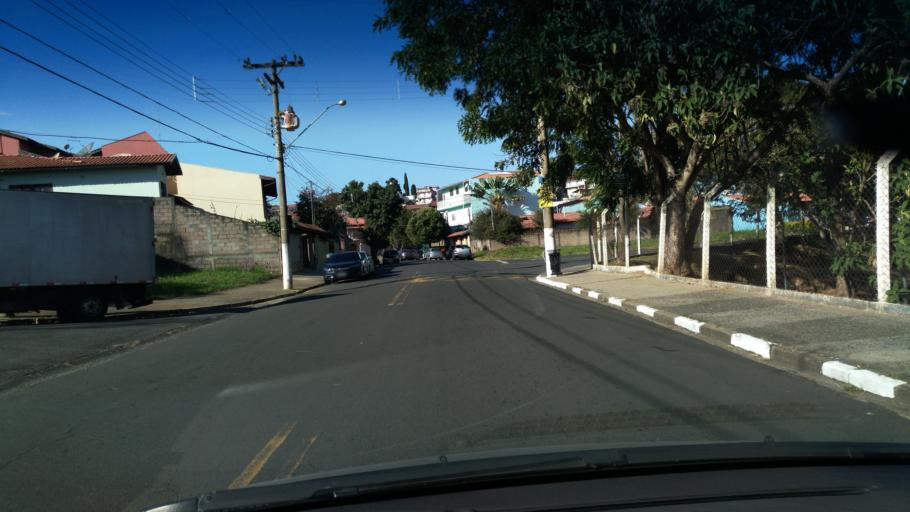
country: BR
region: Sao Paulo
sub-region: Valinhos
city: Valinhos
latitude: -22.9543
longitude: -46.9817
